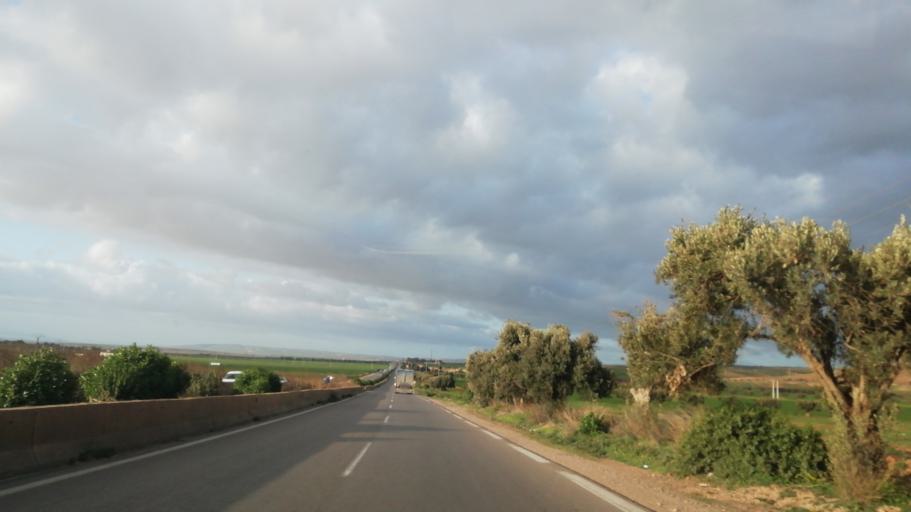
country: DZ
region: Oran
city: Bou Tlelis
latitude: 35.5550
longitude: -0.9444
